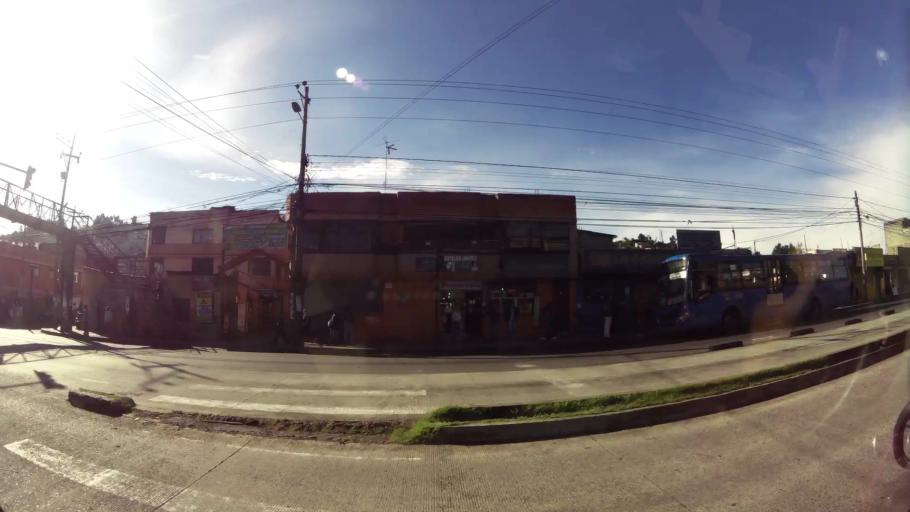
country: EC
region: Pichincha
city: Quito
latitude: -0.2837
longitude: -78.5358
